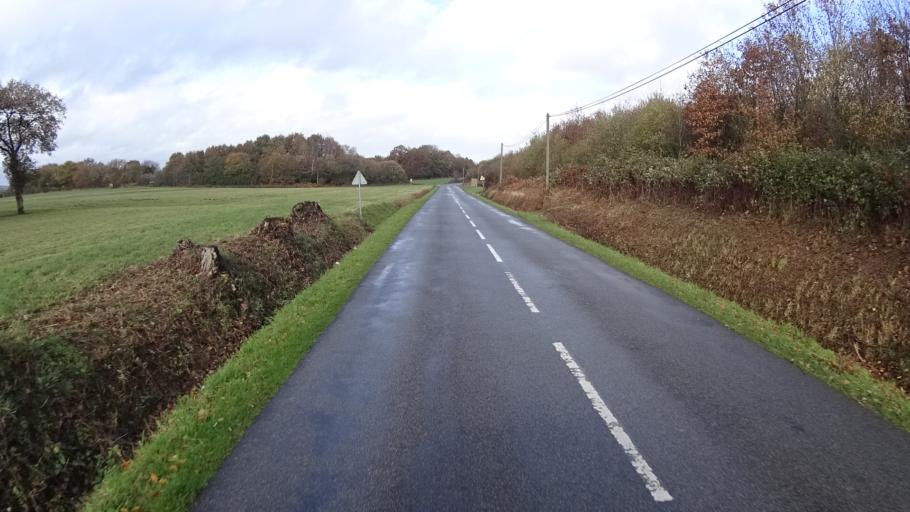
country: FR
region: Pays de la Loire
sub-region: Departement de la Loire-Atlantique
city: Saint-Nicolas-de-Redon
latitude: 47.6169
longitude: -2.0682
